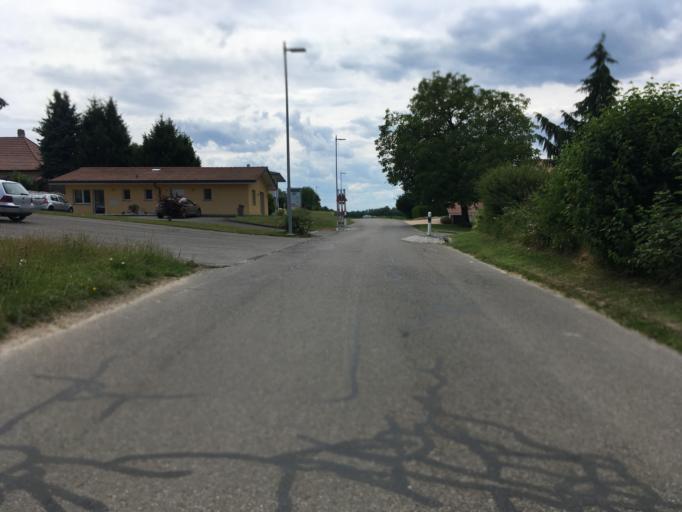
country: CH
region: Fribourg
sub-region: Broye District
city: Estavayer-le-Lac
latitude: 46.8729
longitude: 6.8847
